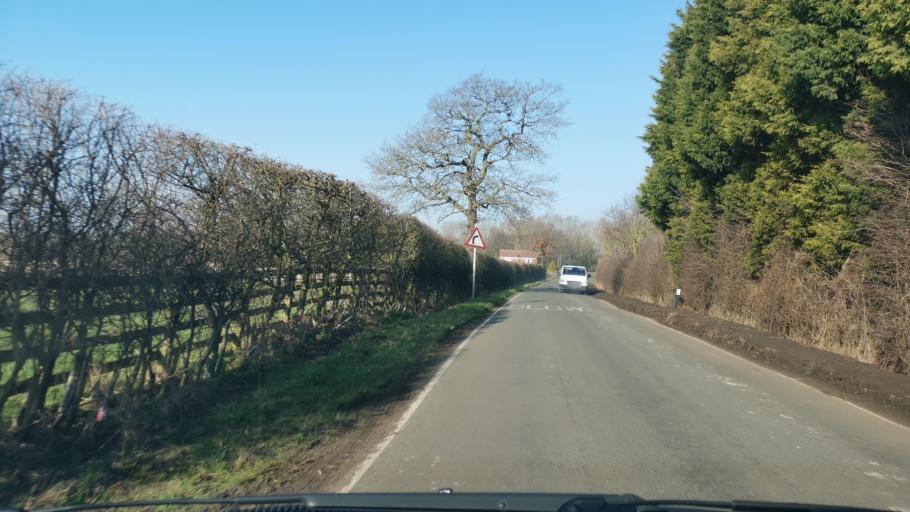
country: GB
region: England
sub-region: City of York
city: Murton
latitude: 53.9755
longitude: -1.0161
